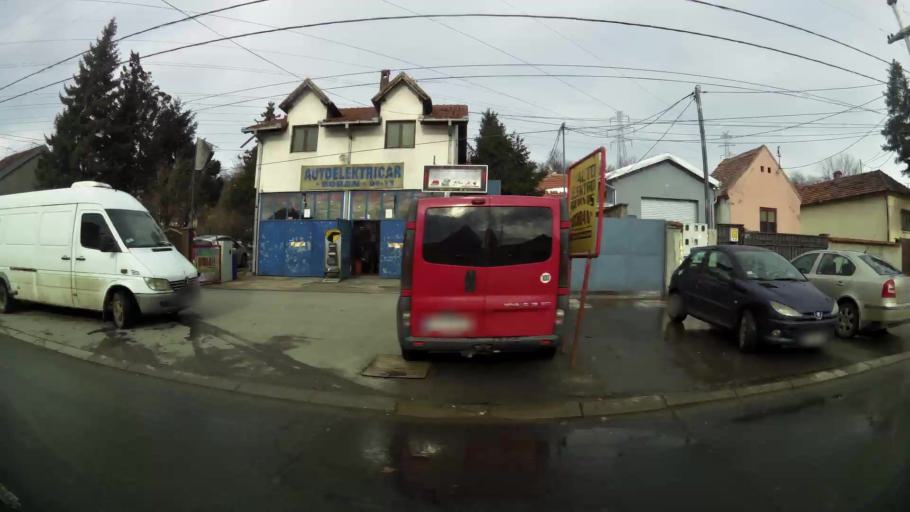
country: RS
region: Central Serbia
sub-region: Belgrade
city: Zemun
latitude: 44.8023
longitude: 20.3620
